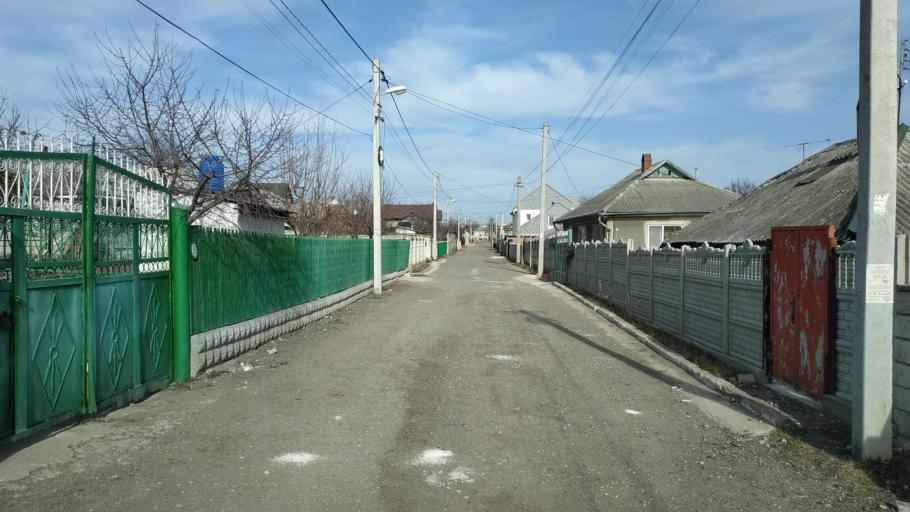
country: MD
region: Chisinau
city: Vatra
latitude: 47.0755
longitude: 28.6851
